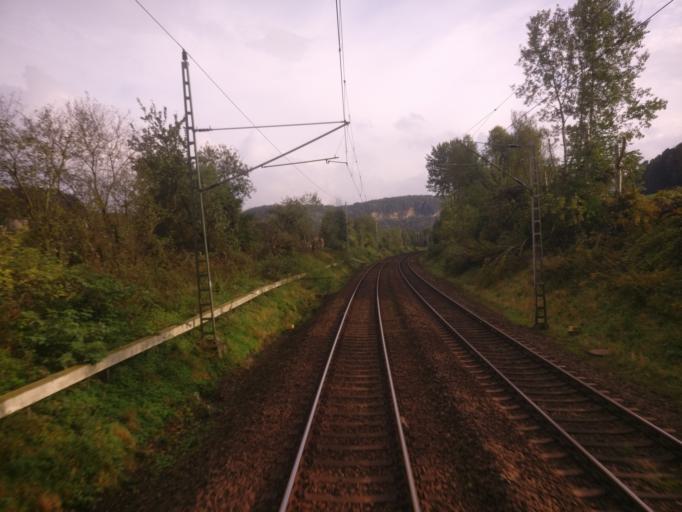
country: DE
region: Saxony
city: Konigstein
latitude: 50.9527
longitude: 14.0813
